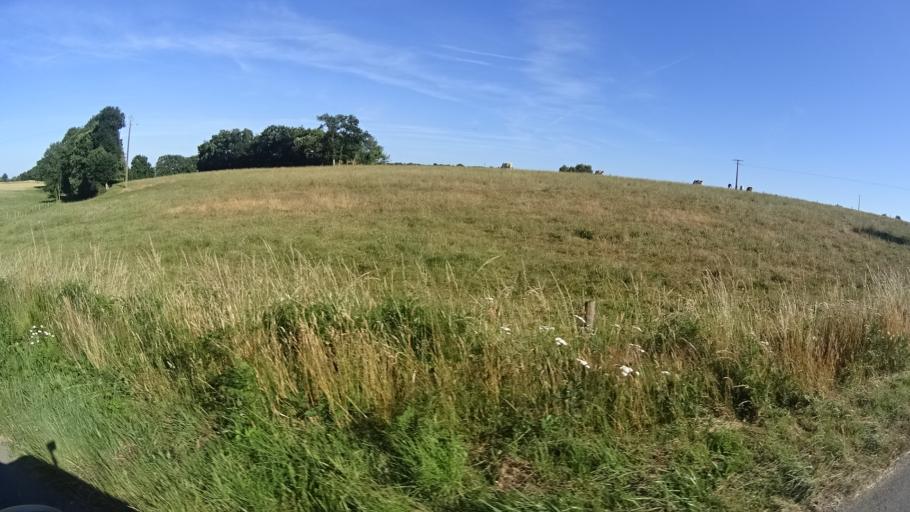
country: FR
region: Brittany
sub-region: Departement d'Ille-et-Vilaine
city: Langon
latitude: 47.7143
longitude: -1.8563
